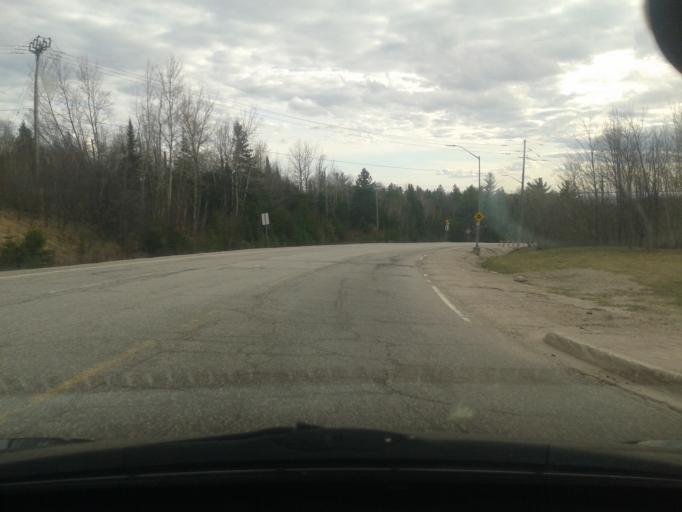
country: CA
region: Ontario
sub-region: Nipissing District
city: North Bay
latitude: 46.3419
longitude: -79.4876
